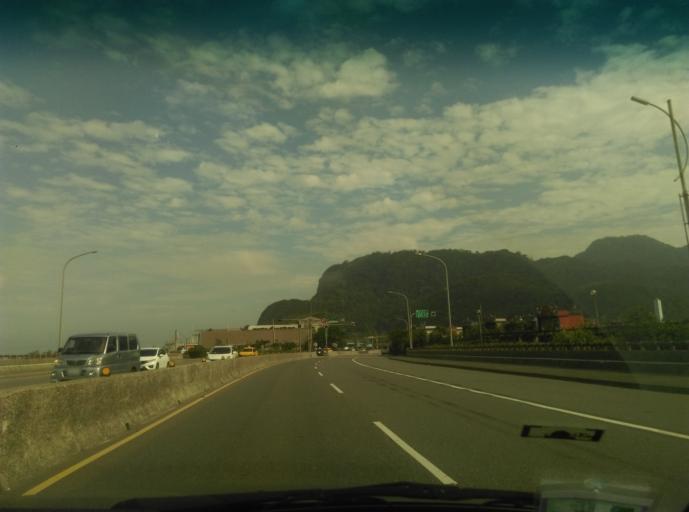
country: TW
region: Taiwan
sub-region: Keelung
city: Keelung
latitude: 25.1800
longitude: 121.6927
